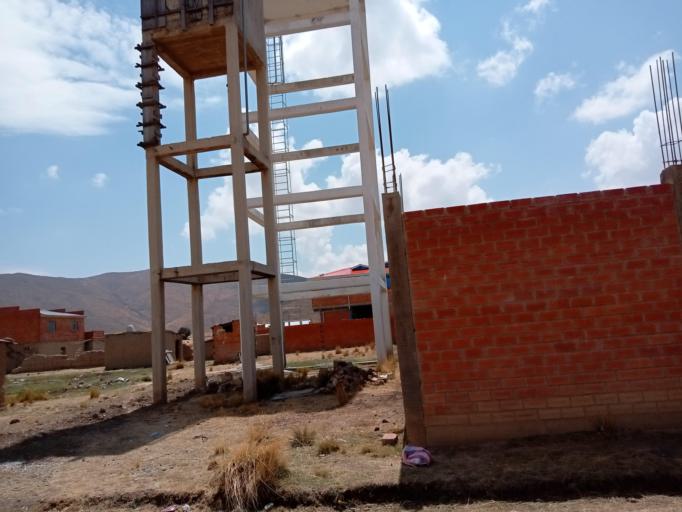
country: BO
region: La Paz
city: Batallas
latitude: -16.4074
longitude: -68.5437
